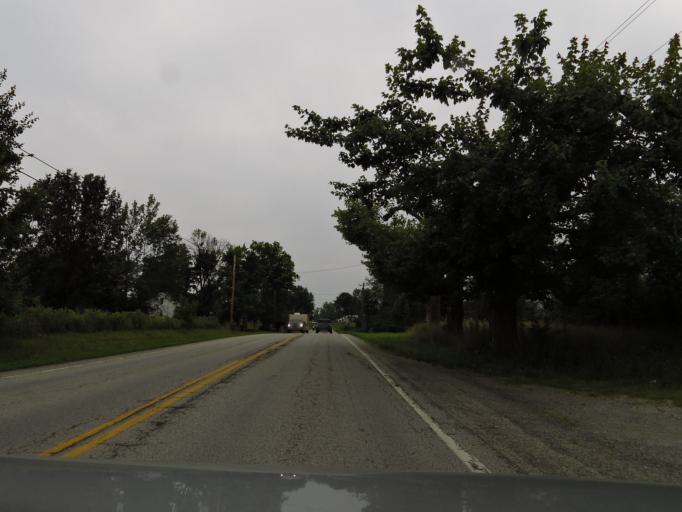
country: US
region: Ohio
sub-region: Brown County
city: Mount Orab
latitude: 39.0589
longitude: -83.9246
